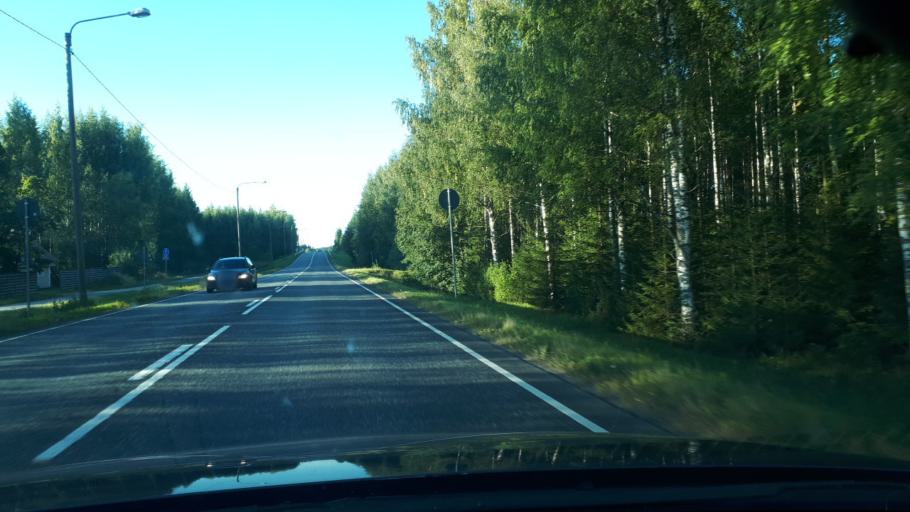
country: FI
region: Northern Savo
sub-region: Ylae-Savo
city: Lapinlahti
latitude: 63.4286
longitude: 27.3286
